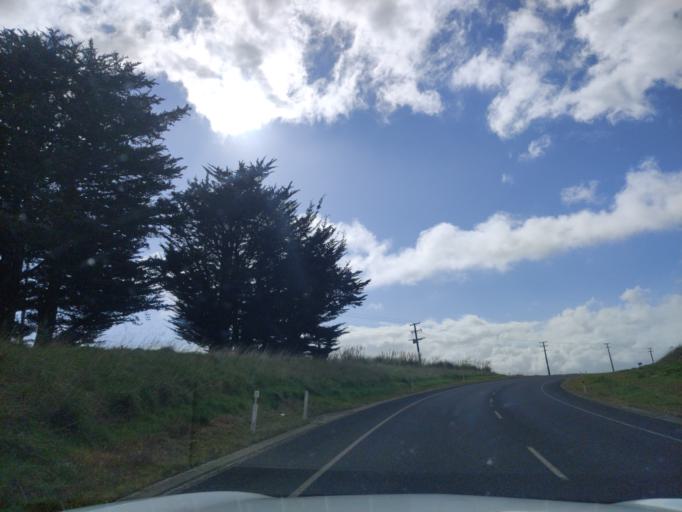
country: NZ
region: Manawatu-Wanganui
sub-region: Palmerston North City
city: Palmerston North
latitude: -40.4137
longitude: 175.5999
